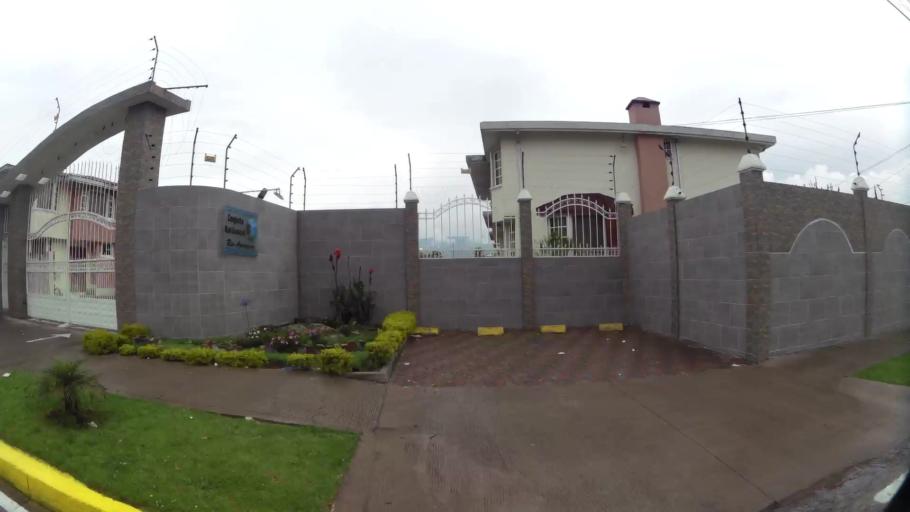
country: EC
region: Pichincha
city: Sangolqui
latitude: -0.2929
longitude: -78.4565
